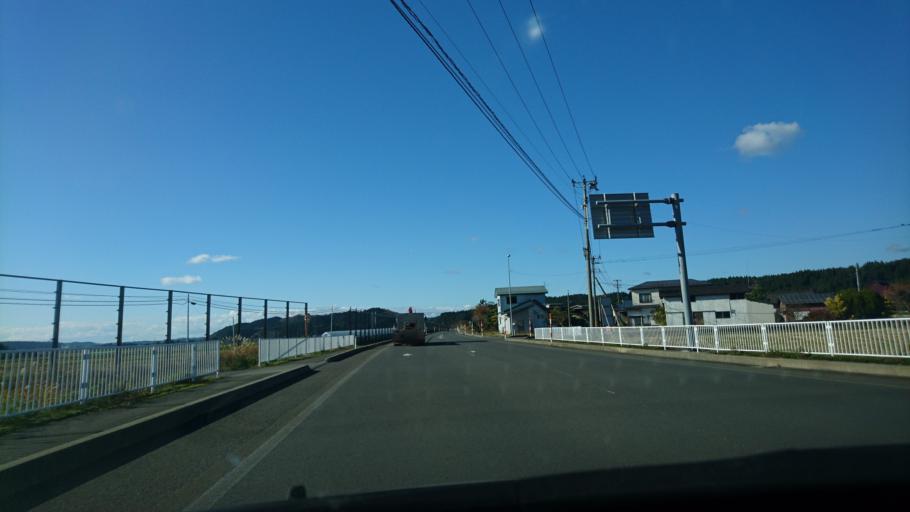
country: JP
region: Akita
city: Akita
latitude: 39.3447
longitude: 140.1185
